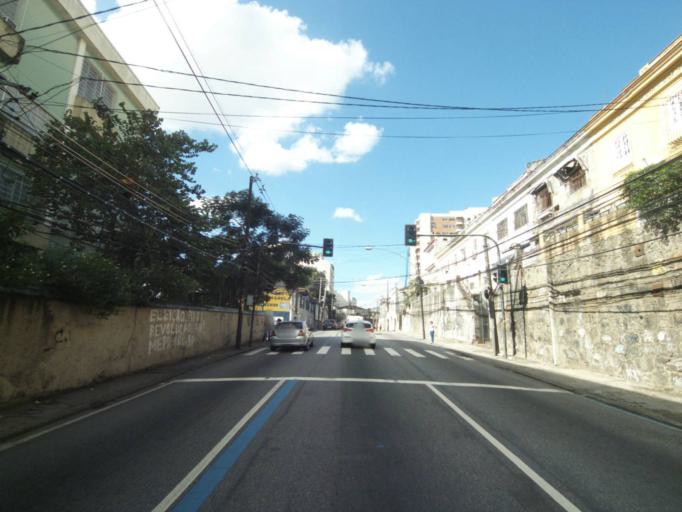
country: BR
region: Rio de Janeiro
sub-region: Rio De Janeiro
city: Rio de Janeiro
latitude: -22.9029
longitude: -43.2501
